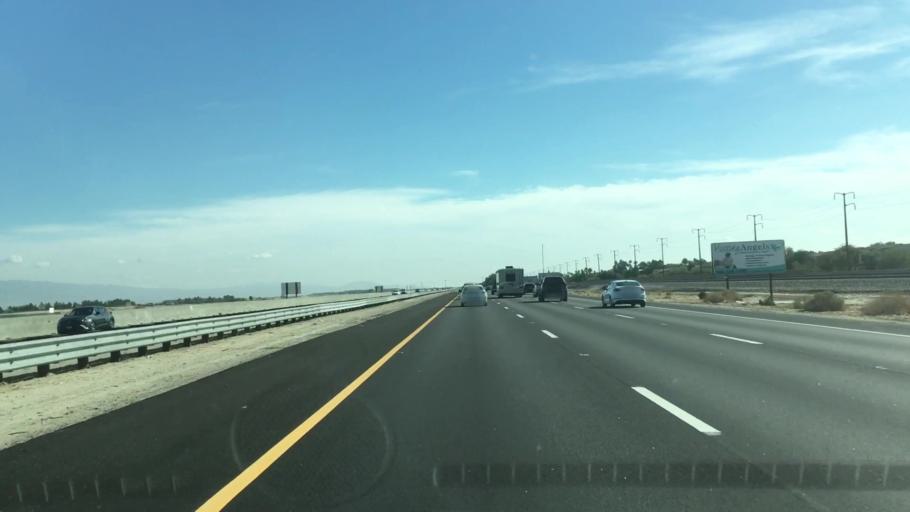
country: US
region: California
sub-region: Riverside County
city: Thousand Palms
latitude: 33.7797
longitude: -116.3442
